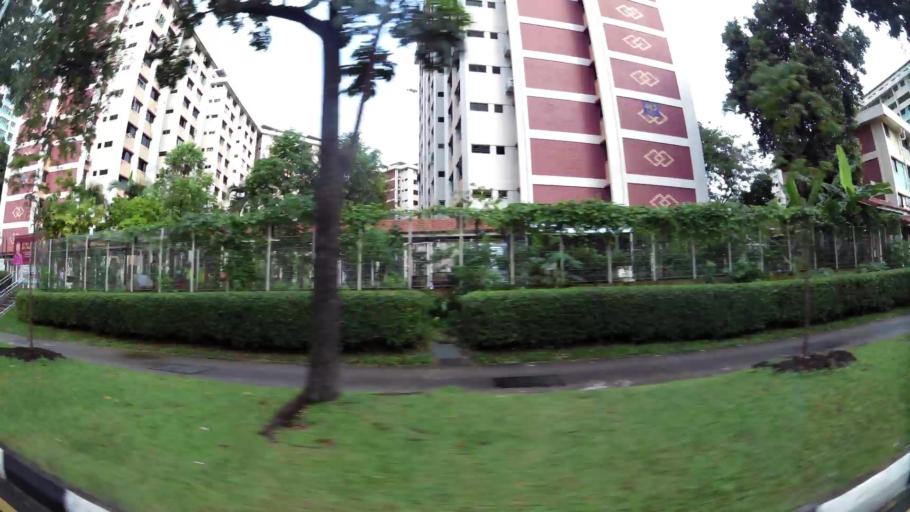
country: SG
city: Singapore
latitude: 1.3672
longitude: 103.8568
